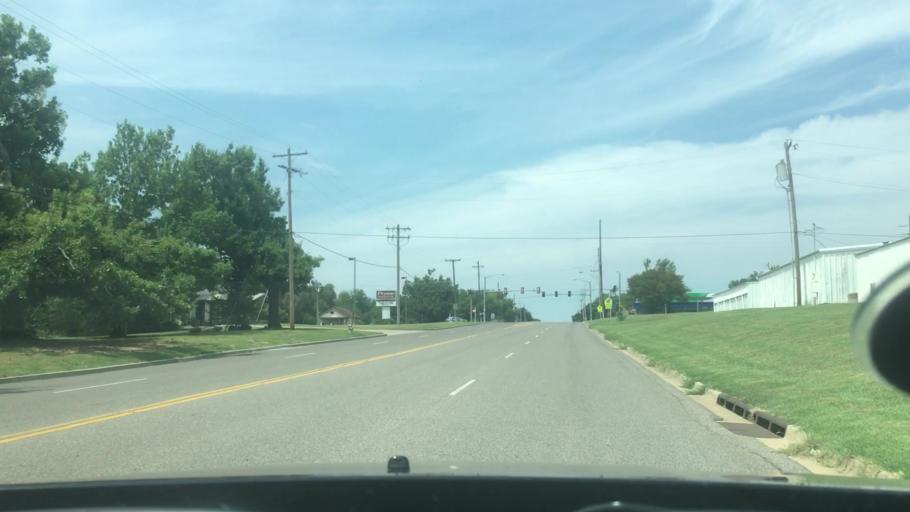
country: US
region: Oklahoma
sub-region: Pottawatomie County
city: Shawnee
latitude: 35.3327
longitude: -96.8921
